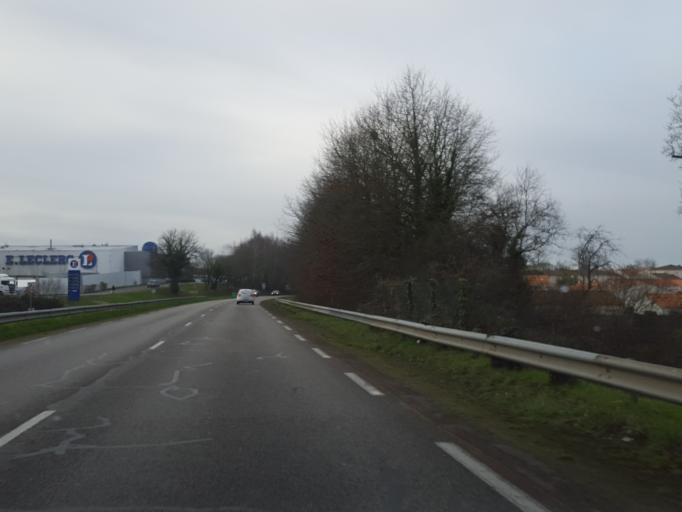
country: FR
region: Pays de la Loire
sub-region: Departement de la Vendee
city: La Roche-sur-Yon
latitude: 46.6739
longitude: -1.4052
